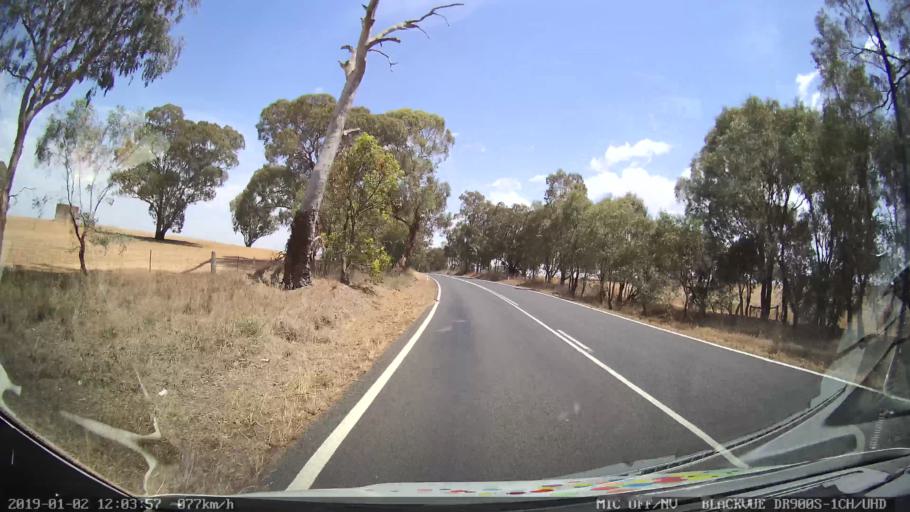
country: AU
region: New South Wales
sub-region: Young
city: Young
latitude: -34.5277
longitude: 148.3166
